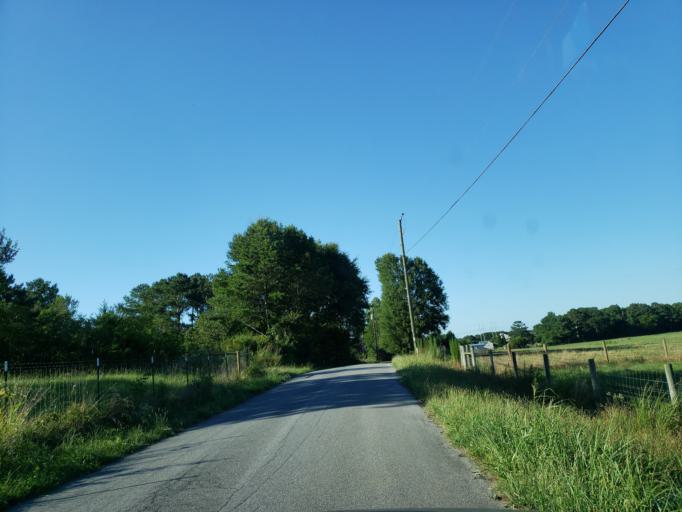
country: US
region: Georgia
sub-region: Bartow County
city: Euharlee
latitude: 34.1125
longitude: -84.9923
